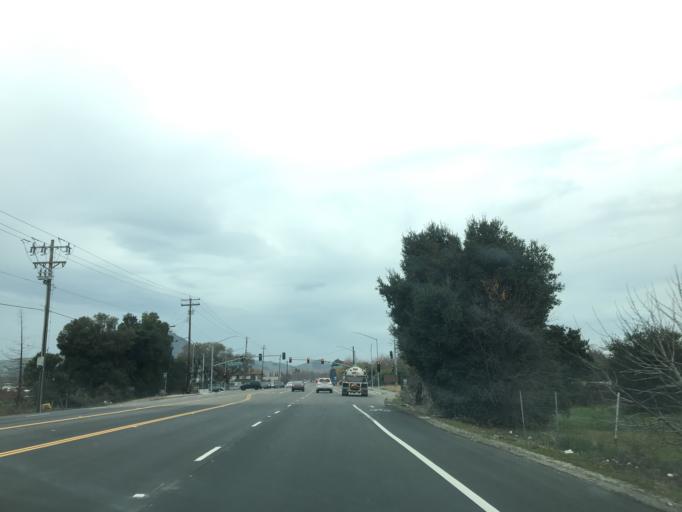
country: US
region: California
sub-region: Santa Clara County
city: Morgan Hill
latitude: 37.1069
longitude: -121.6340
